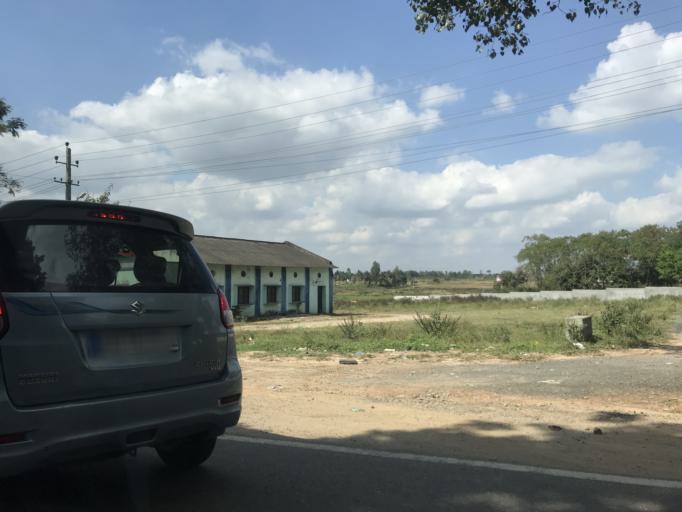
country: IN
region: Karnataka
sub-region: Hassan
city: Hassan
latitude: 12.9936
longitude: 76.0694
